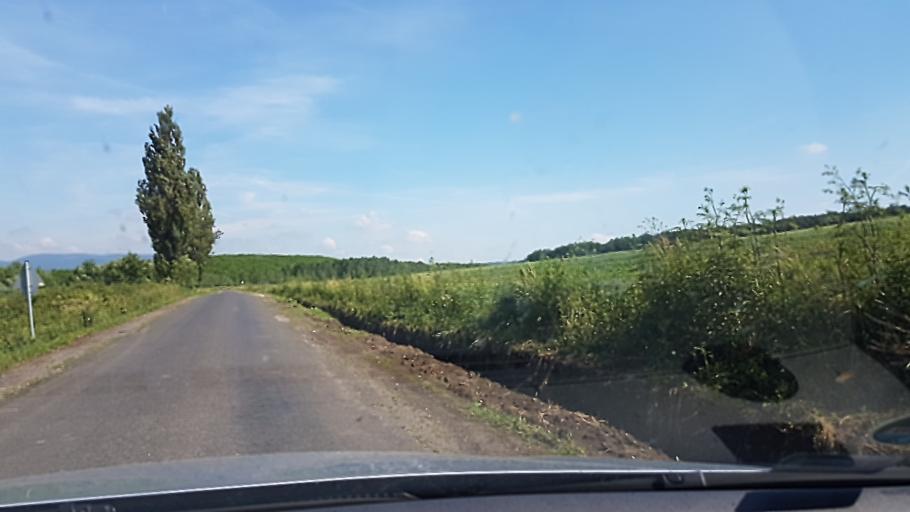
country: HU
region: Borsod-Abauj-Zemplen
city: Saly
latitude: 47.9377
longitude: 20.7100
